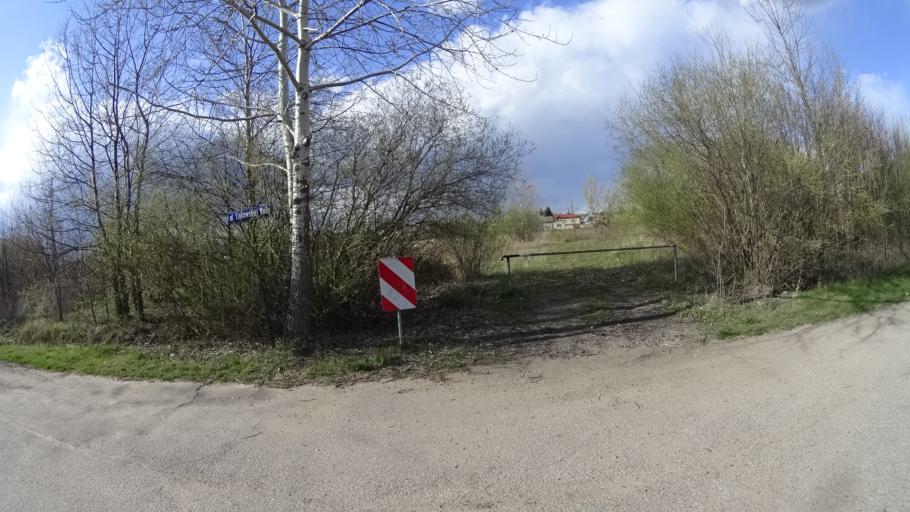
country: PL
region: Masovian Voivodeship
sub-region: Powiat warszawski zachodni
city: Babice
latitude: 52.2856
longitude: 20.8707
